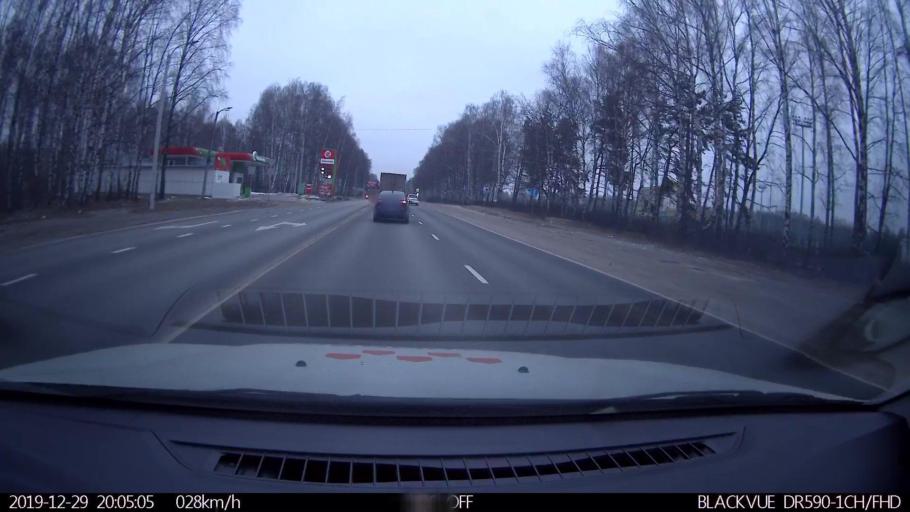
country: RU
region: Nizjnij Novgorod
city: Neklyudovo
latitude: 56.3886
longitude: 44.0112
